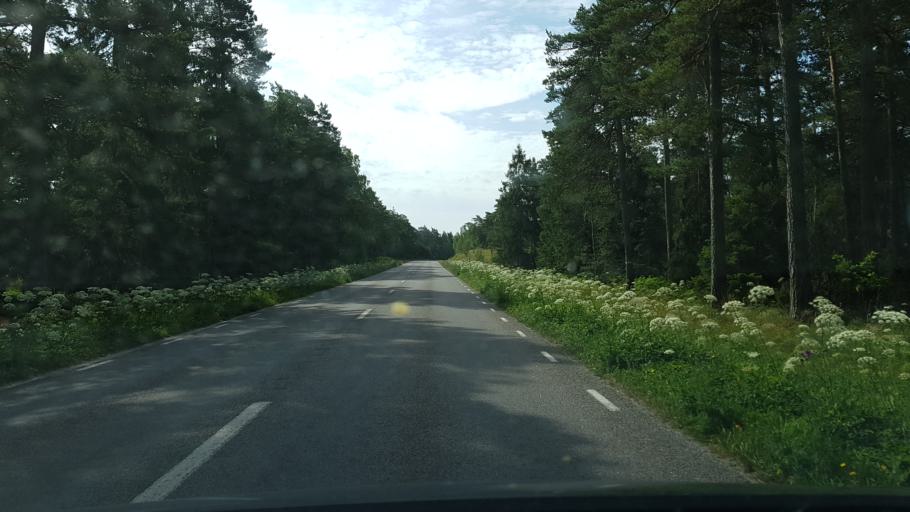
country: SE
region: Gotland
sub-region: Gotland
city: Hemse
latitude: 57.4585
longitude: 18.5753
